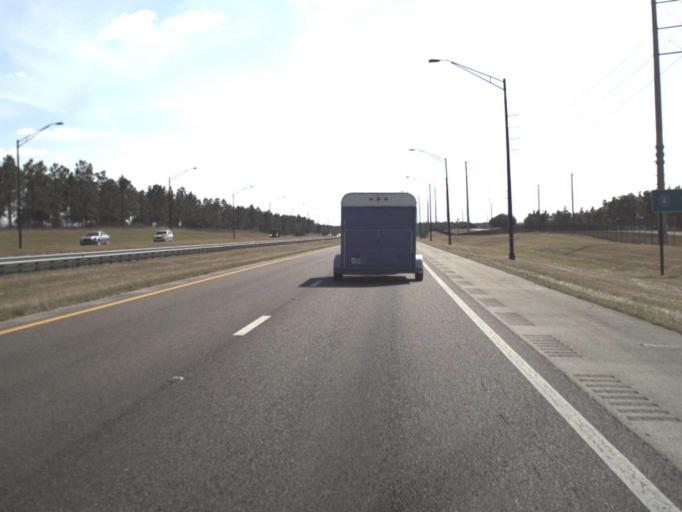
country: US
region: Florida
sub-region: Polk County
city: Citrus Ridge
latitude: 28.4031
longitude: -81.6242
